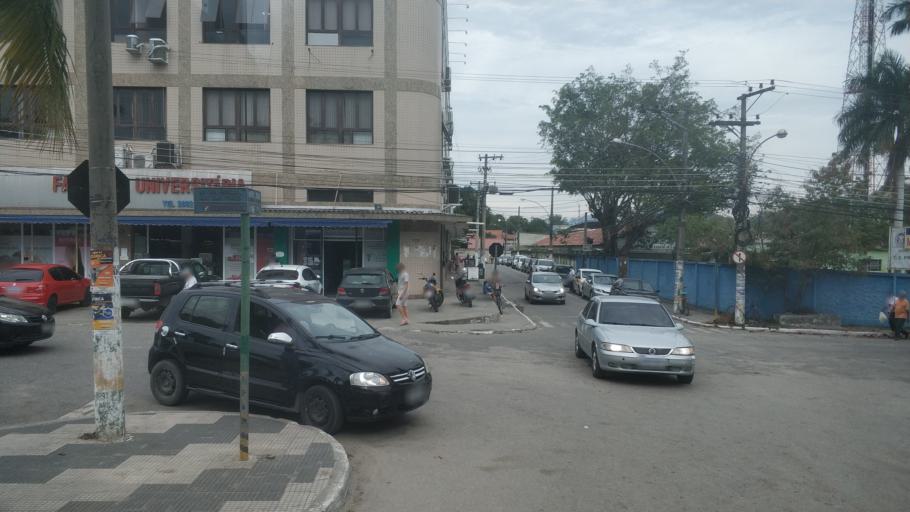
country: BR
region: Rio de Janeiro
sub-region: Seropedica
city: Seropedica
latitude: -22.7427
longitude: -43.7040
